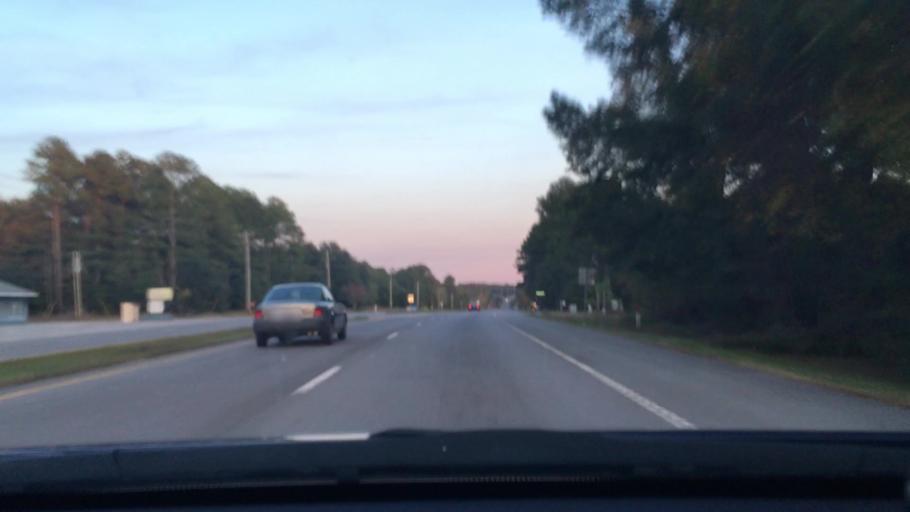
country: US
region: South Carolina
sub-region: Richland County
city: Gadsden
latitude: 33.9436
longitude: -80.7404
